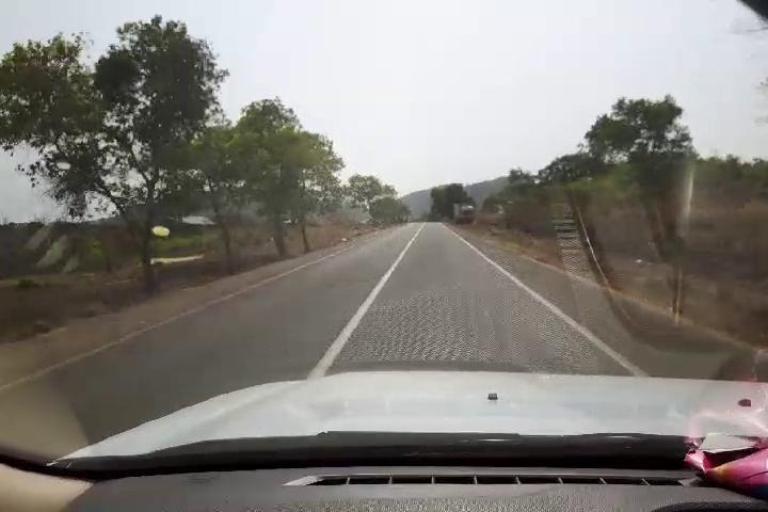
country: SL
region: Western Area
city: Waterloo
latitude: 8.2026
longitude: -13.1273
